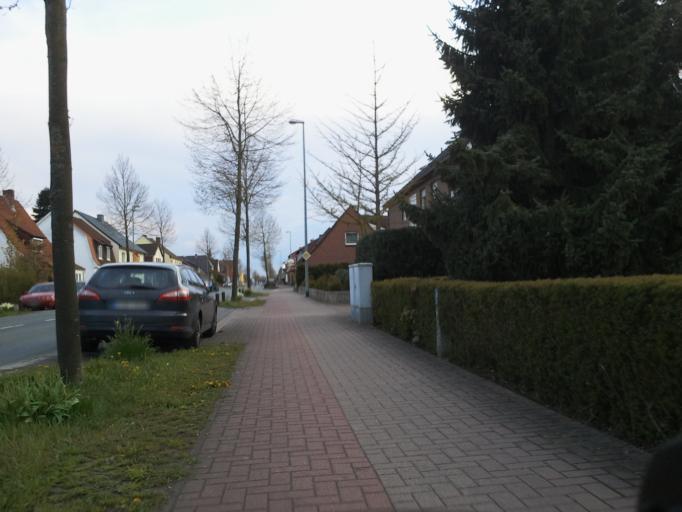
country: DE
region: Lower Saxony
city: Nienburg
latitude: 52.6573
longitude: 9.2299
